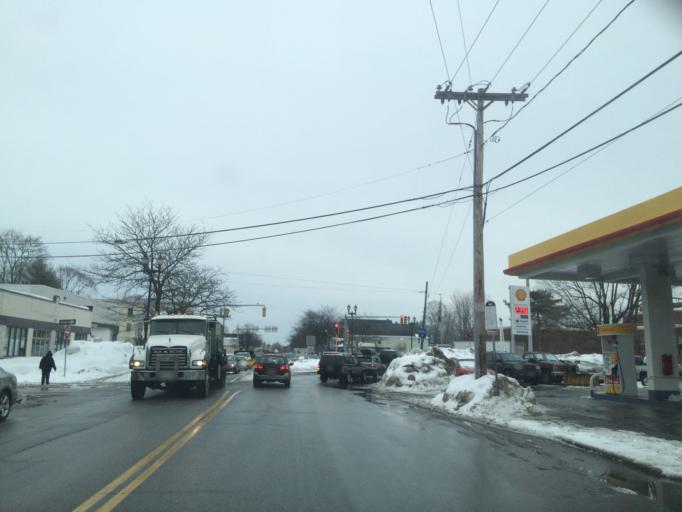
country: US
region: Massachusetts
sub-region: Middlesex County
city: Waltham
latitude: 42.3763
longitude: -71.2506
